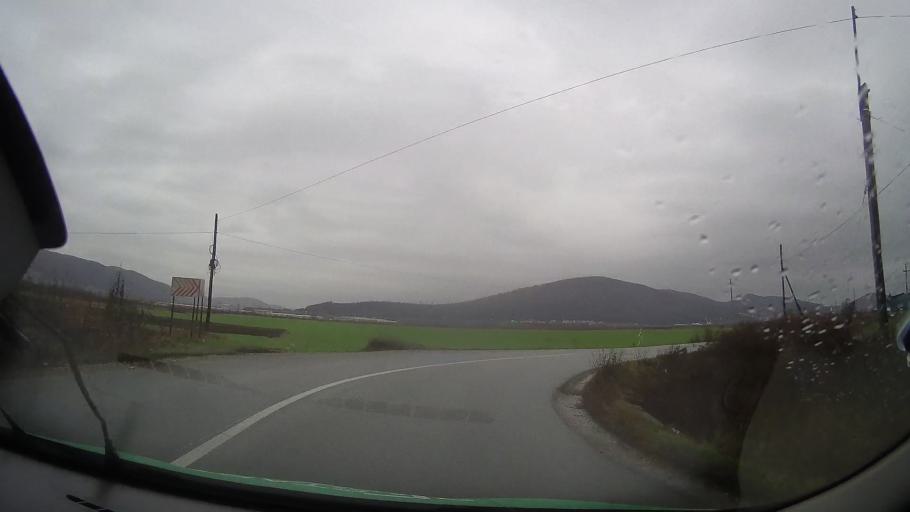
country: RO
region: Bistrita-Nasaud
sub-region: Municipiul Bistrita
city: Viisoara
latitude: 47.0581
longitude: 24.4359
